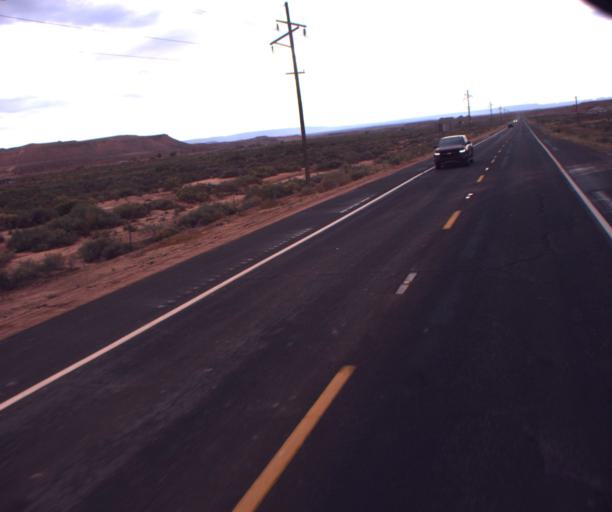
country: US
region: Arizona
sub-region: Coconino County
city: Tuba City
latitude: 36.1062
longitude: -111.2593
